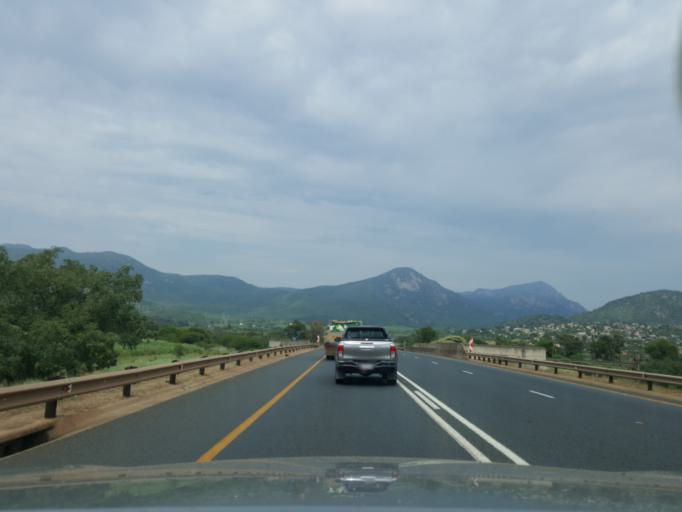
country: SZ
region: Hhohho
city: Ntfonjeni
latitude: -25.5374
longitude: 31.3242
